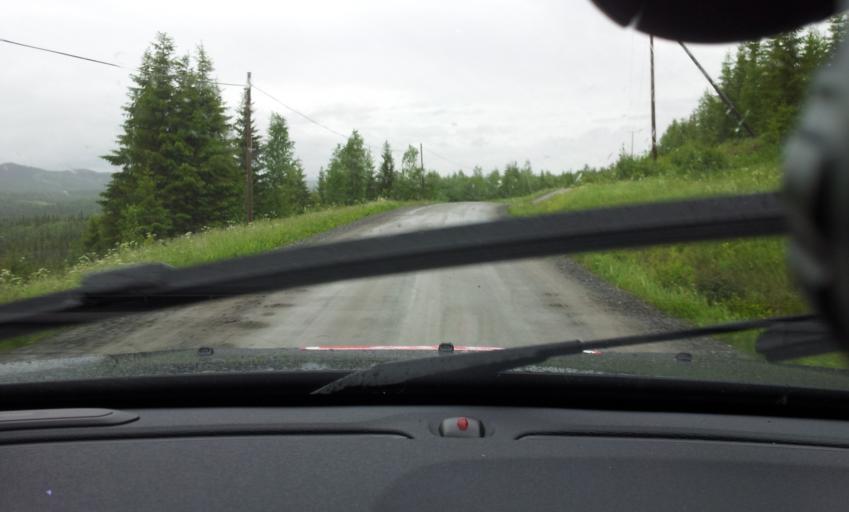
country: SE
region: Jaemtland
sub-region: Are Kommun
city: Are
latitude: 63.4116
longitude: 12.8291
